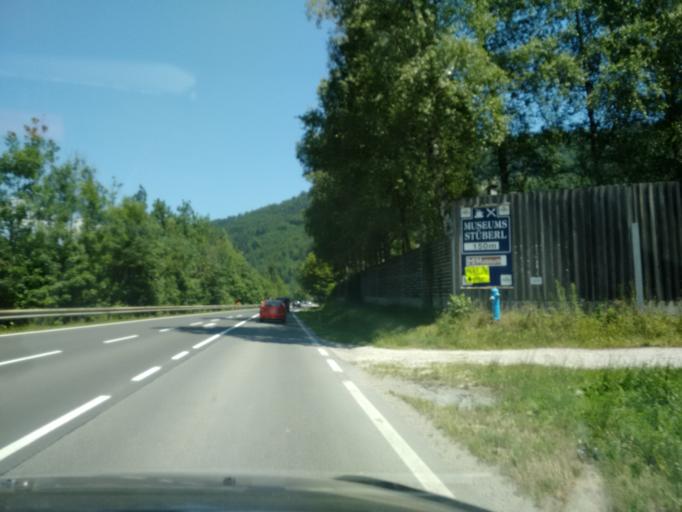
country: AT
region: Upper Austria
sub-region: Politischer Bezirk Gmunden
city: Bad Ischl
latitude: 47.6830
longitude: 13.6221
